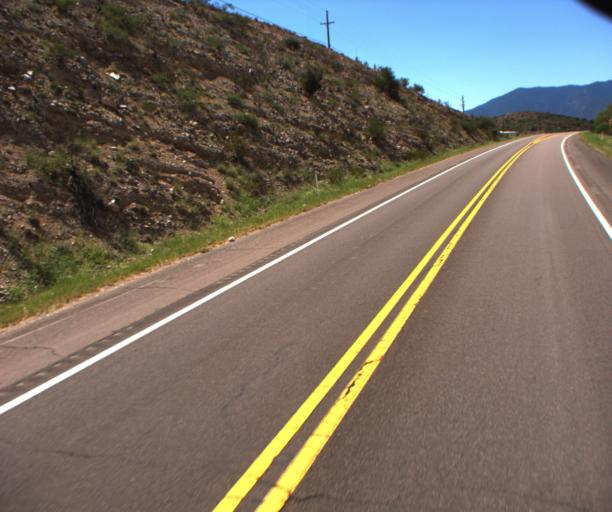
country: US
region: Arizona
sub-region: Gila County
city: Globe
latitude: 33.4052
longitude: -110.7442
